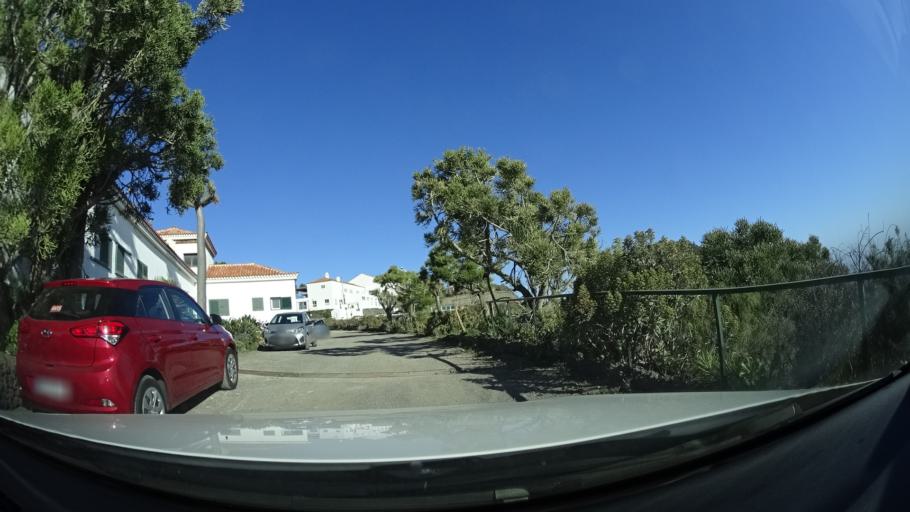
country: ES
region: Canary Islands
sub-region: Provincia de Las Palmas
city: Santa Brigida
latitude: 28.0303
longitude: -15.4594
